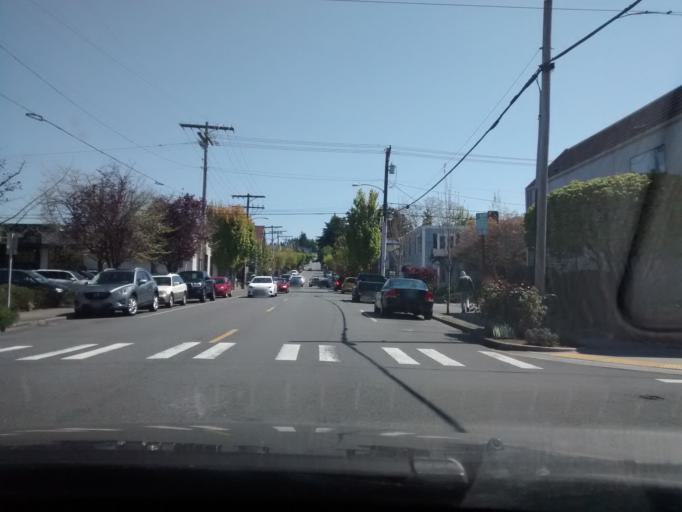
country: US
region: Washington
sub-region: Snohomish County
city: Edmonds
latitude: 47.8097
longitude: -122.3789
